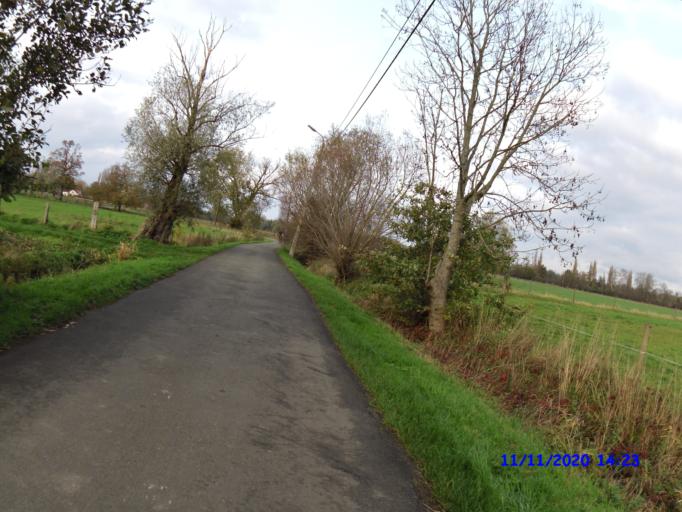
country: BE
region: Flanders
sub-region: Provincie Oost-Vlaanderen
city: Dendermonde
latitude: 51.0225
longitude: 4.0847
